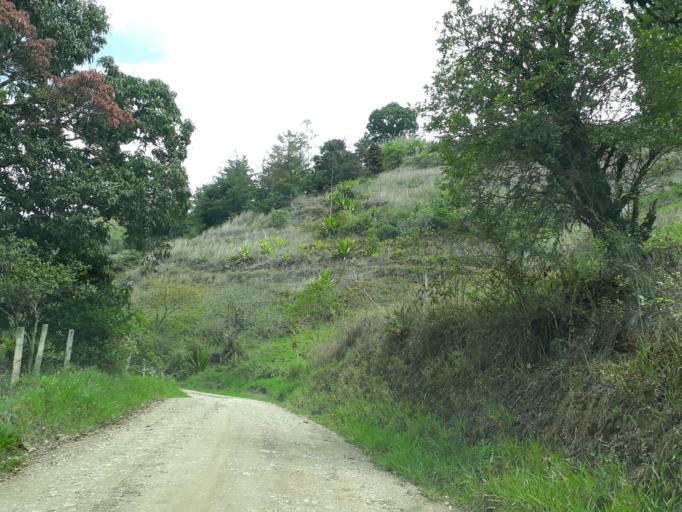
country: CO
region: Cundinamarca
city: Manta
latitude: 5.0055
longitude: -73.5202
